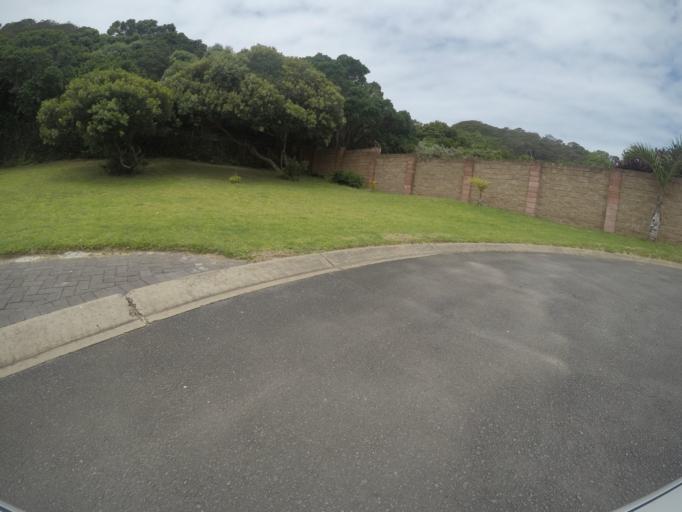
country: ZA
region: Eastern Cape
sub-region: Buffalo City Metropolitan Municipality
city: East London
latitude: -32.9778
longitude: 27.9564
